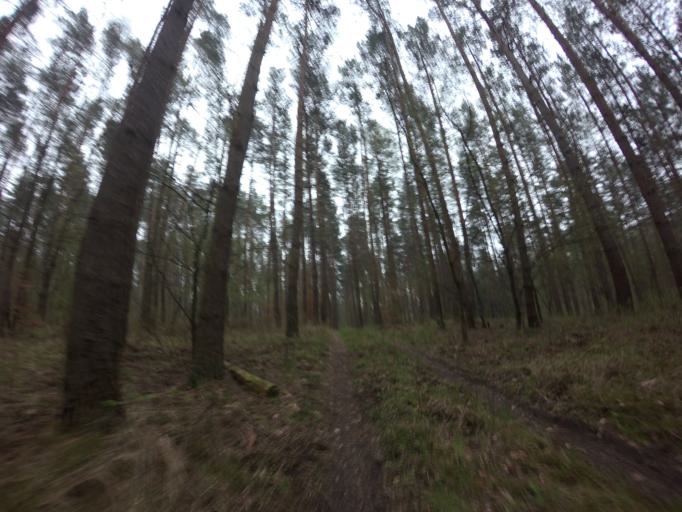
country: PL
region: West Pomeranian Voivodeship
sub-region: Powiat choszczenski
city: Recz
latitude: 53.1865
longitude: 15.5324
